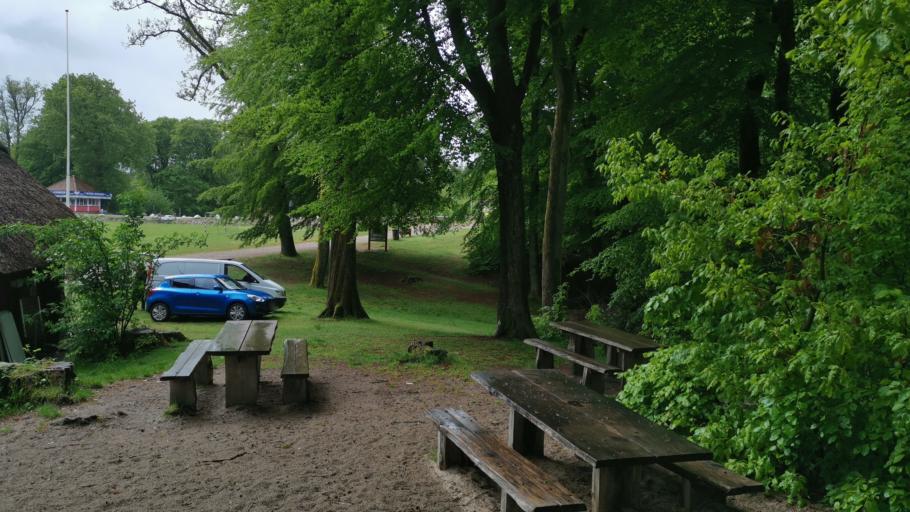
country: DK
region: Central Jutland
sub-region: Silkeborg Kommune
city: Svejbaek
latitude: 56.1040
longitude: 9.6868
